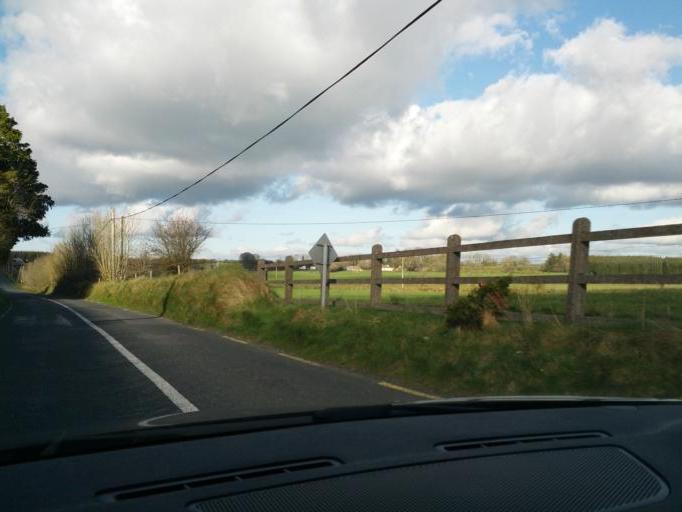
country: IE
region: Connaught
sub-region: Roscommon
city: Castlerea
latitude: 53.6495
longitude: -8.5196
